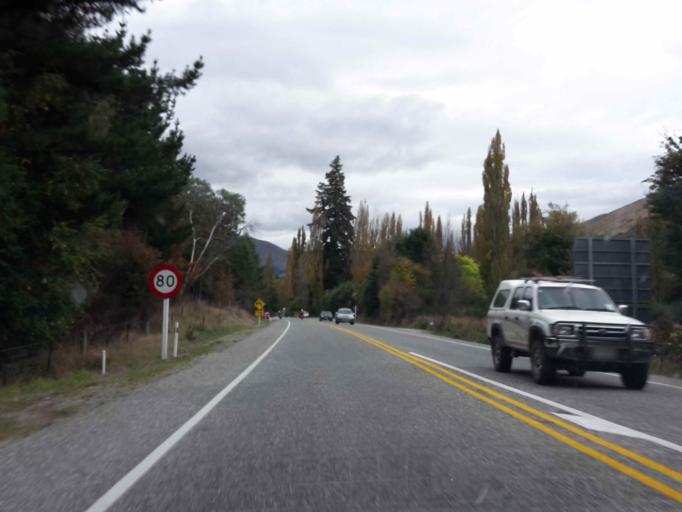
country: NZ
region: Otago
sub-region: Queenstown-Lakes District
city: Arrowtown
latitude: -44.9802
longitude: 168.8544
